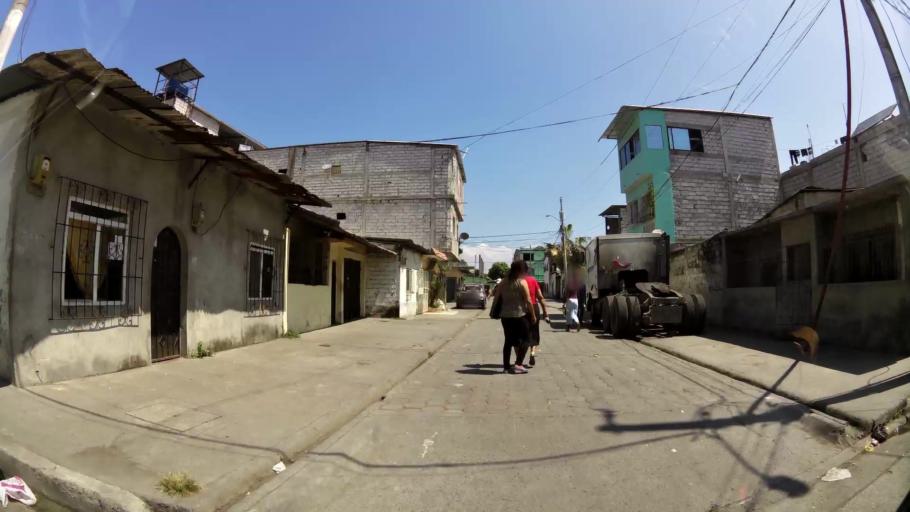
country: EC
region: Guayas
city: Guayaquil
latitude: -2.2385
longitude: -79.9162
